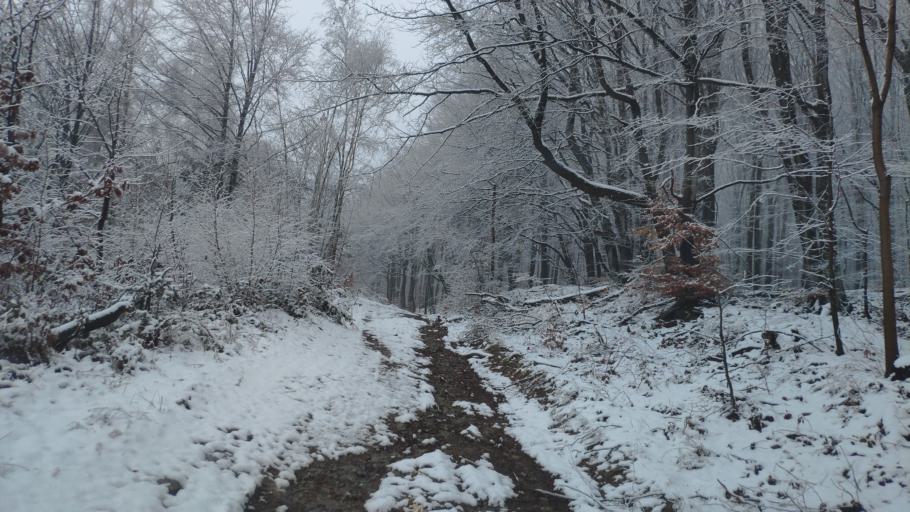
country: SK
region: Kosicky
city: Moldava nad Bodvou
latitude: 48.7435
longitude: 21.0822
